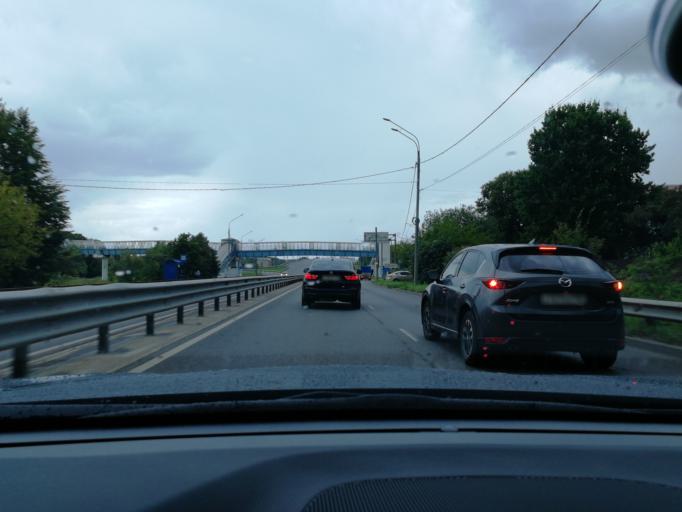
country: RU
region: Moskovskaya
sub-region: Podol'skiy Rayon
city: Podol'sk
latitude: 55.4030
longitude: 37.5515
